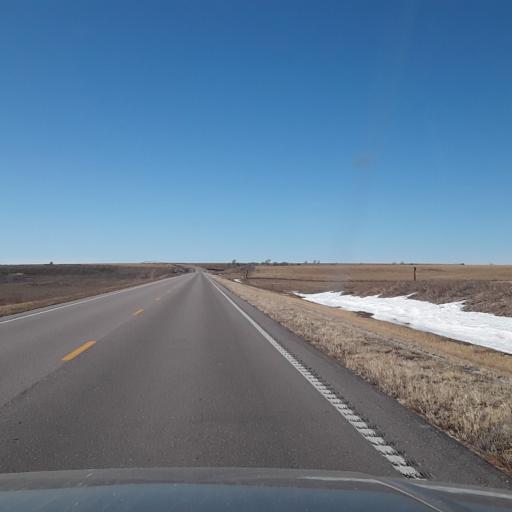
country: US
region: Nebraska
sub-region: Frontier County
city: Stockville
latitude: 40.7057
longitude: -100.2291
